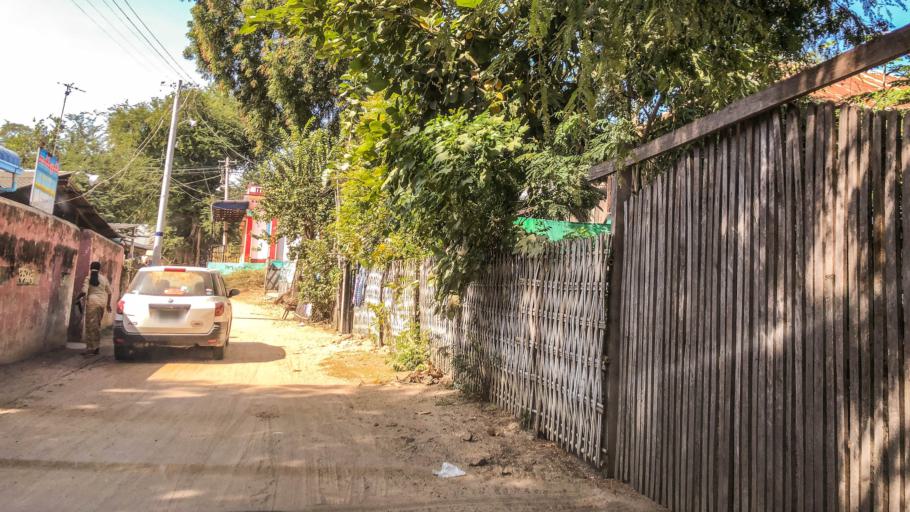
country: MM
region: Magway
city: Magway
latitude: 19.9773
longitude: 95.0331
